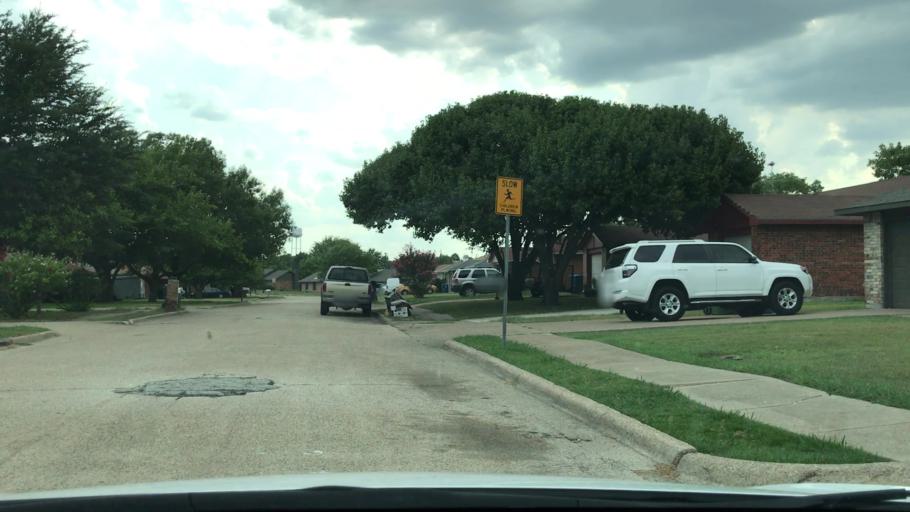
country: US
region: Texas
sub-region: Dallas County
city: Sachse
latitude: 32.9785
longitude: -96.5852
